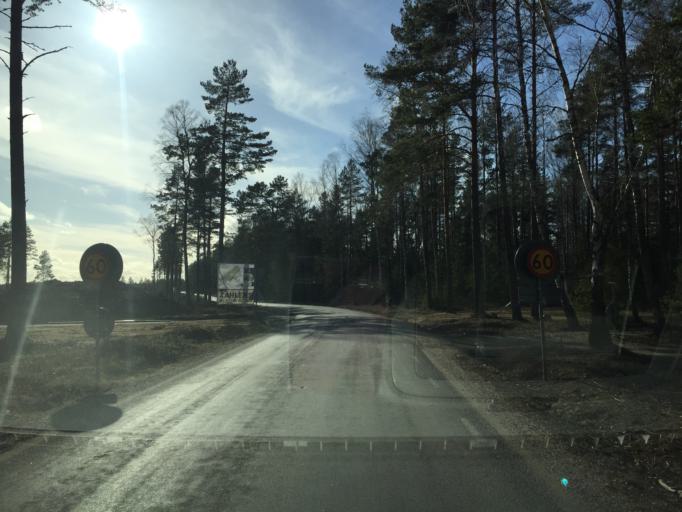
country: SE
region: Stockholm
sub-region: Nynashamns Kommun
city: Osmo
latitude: 59.0500
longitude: 17.8535
